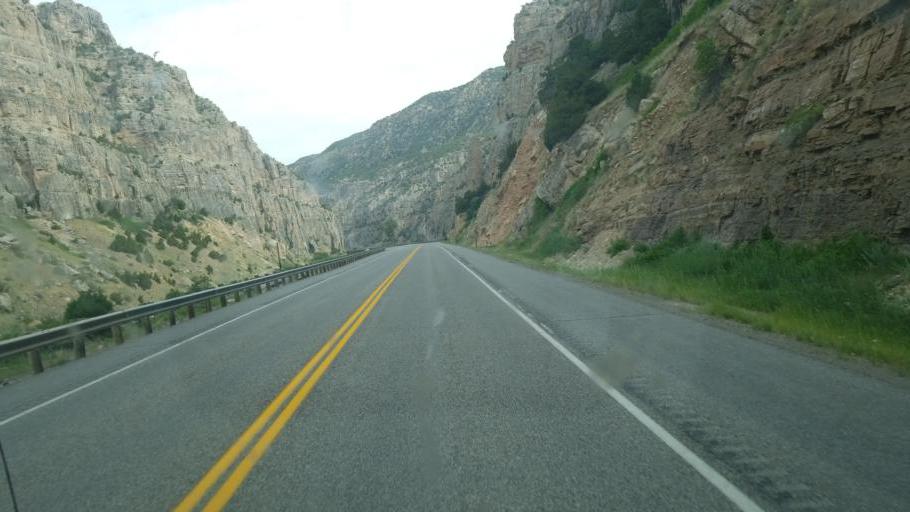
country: US
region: Wyoming
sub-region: Hot Springs County
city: Thermopolis
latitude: 43.5315
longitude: -108.1784
